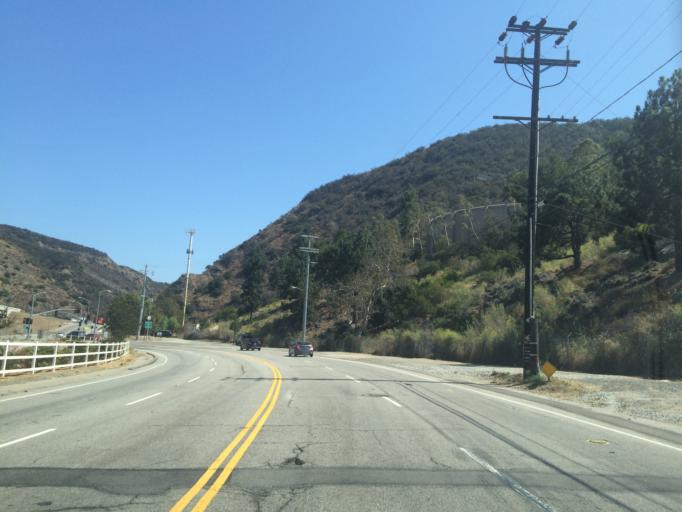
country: US
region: California
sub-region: Los Angeles County
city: Sherman Oaks
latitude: 34.0979
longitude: -118.4789
